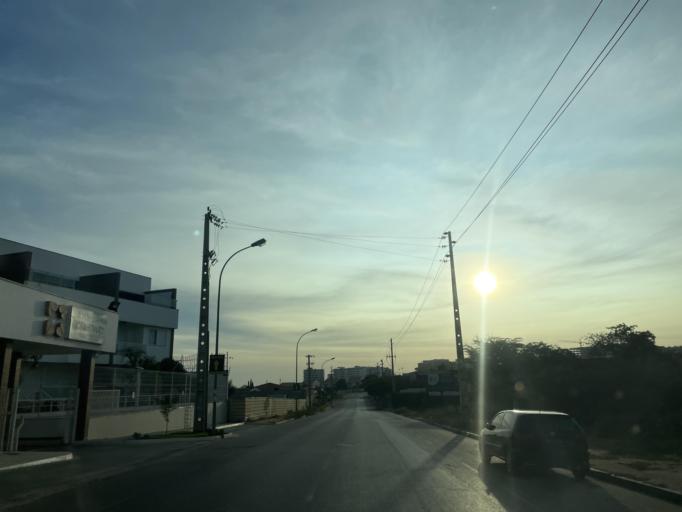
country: AO
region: Luanda
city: Luanda
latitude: -8.9220
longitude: 13.2011
